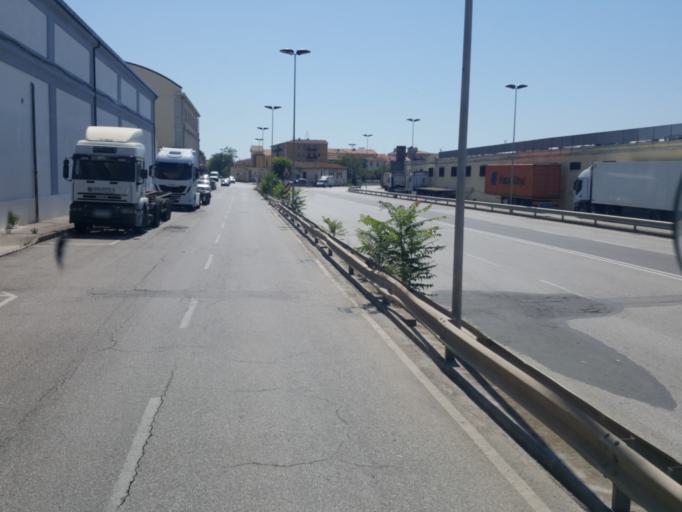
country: IT
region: Tuscany
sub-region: Provincia di Livorno
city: Livorno
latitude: 43.5641
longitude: 10.3128
